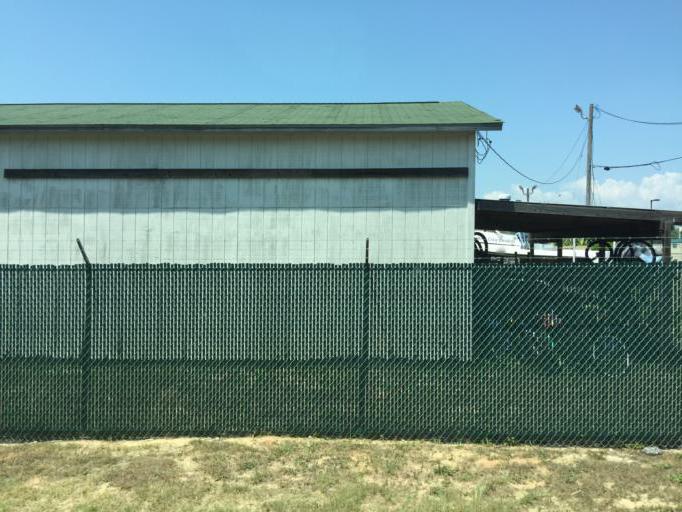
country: US
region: Florida
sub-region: Bay County
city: Laguna Beach
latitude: 30.2288
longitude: -85.8901
